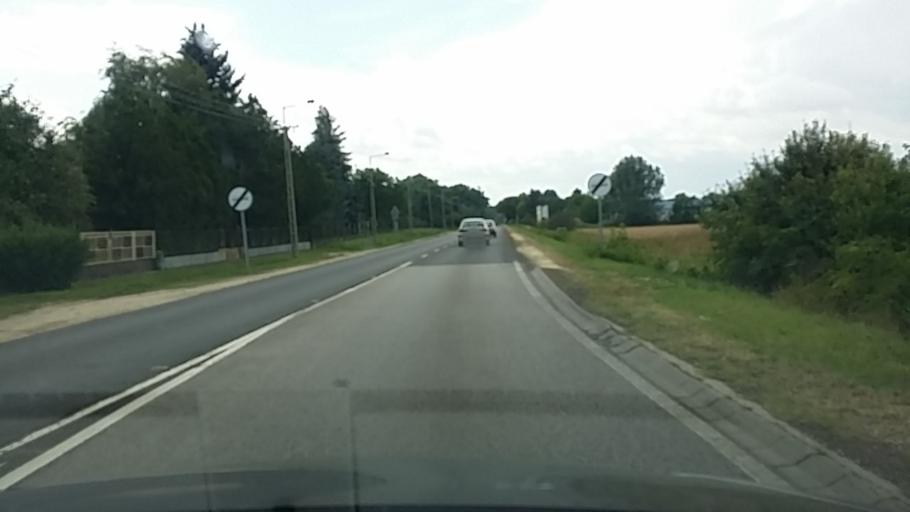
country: HU
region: Pest
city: Orkeny
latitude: 47.1215
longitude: 19.4383
